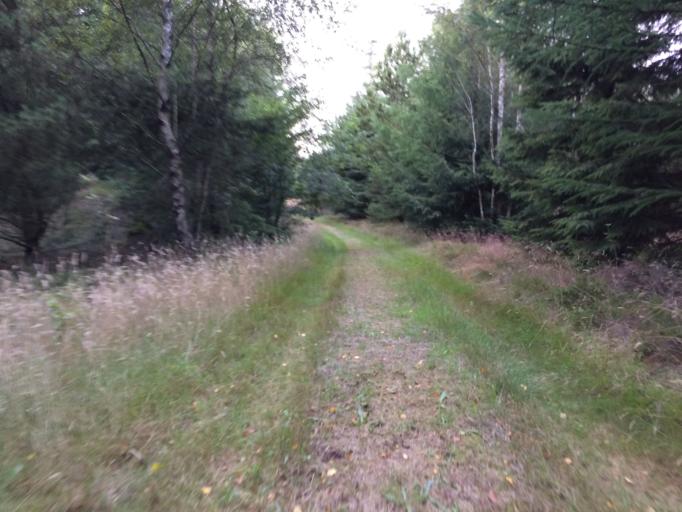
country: DK
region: Central Jutland
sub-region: Holstebro Kommune
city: Ulfborg
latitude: 56.2522
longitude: 8.3733
